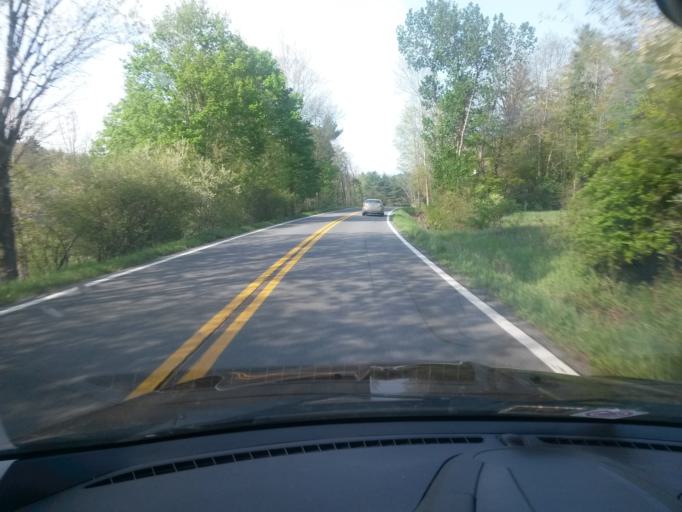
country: US
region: West Virginia
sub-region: Pocahontas County
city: Marlinton
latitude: 38.0576
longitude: -80.0122
